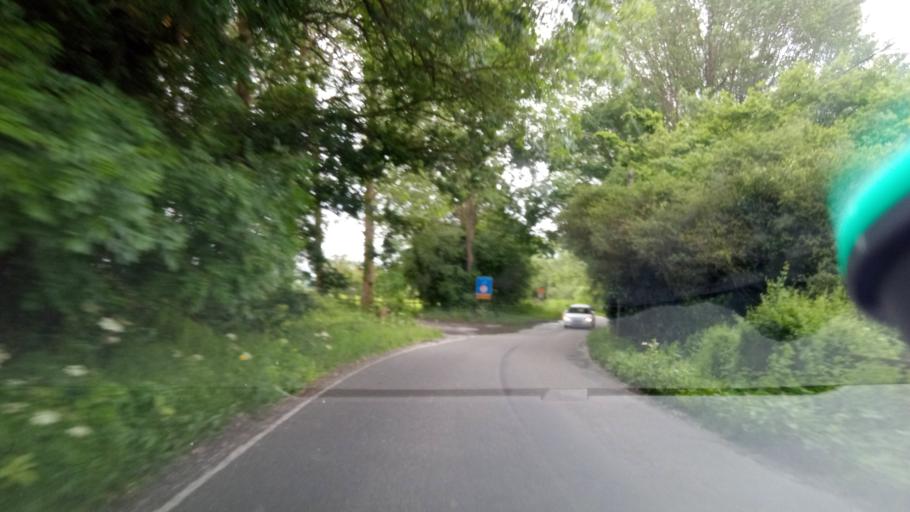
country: GB
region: England
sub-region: Derbyshire
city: Findern
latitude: 52.8636
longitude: -1.5287
